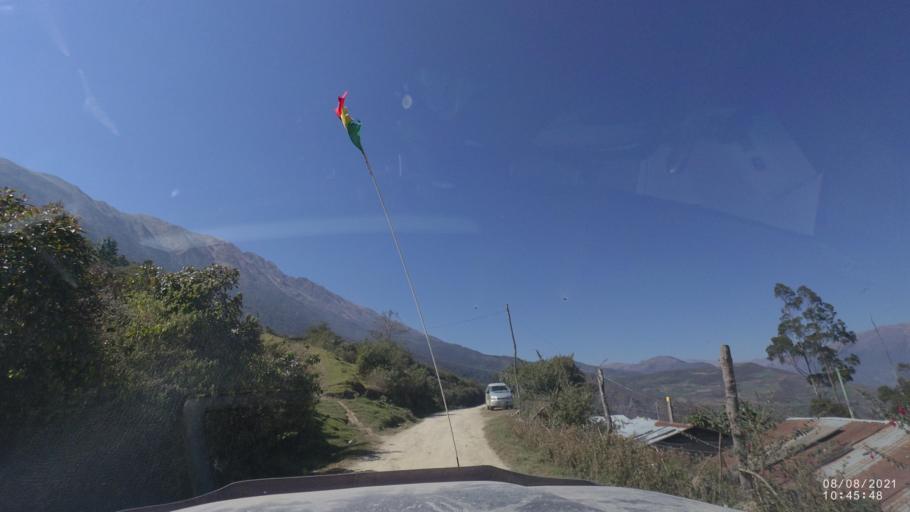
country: BO
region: La Paz
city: Quime
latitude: -16.7054
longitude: -66.7148
